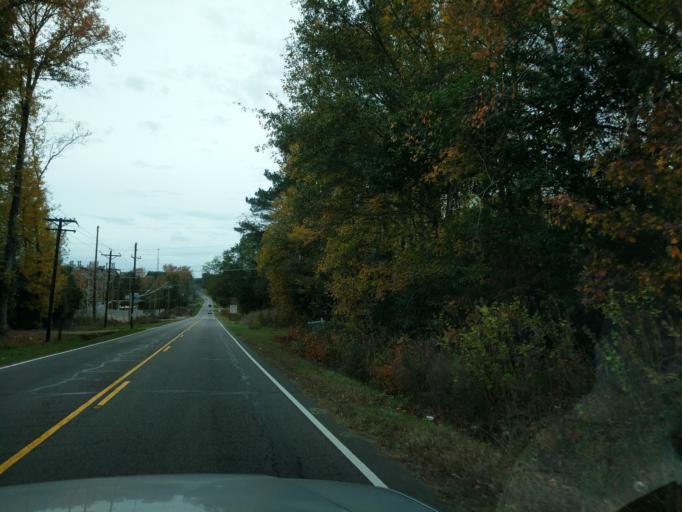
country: US
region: South Carolina
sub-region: Lexington County
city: Batesburg
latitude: 33.9132
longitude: -81.5626
